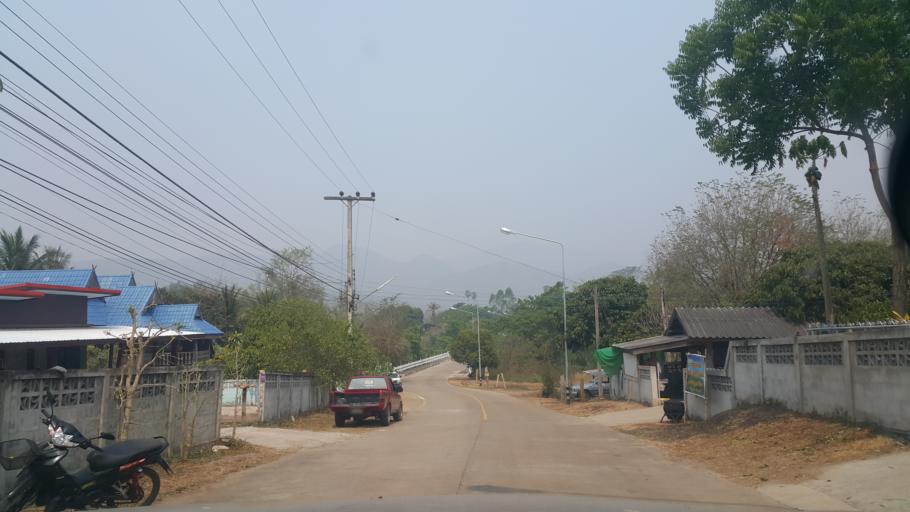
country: TH
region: Lampang
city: Thoen
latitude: 17.7509
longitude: 99.2319
